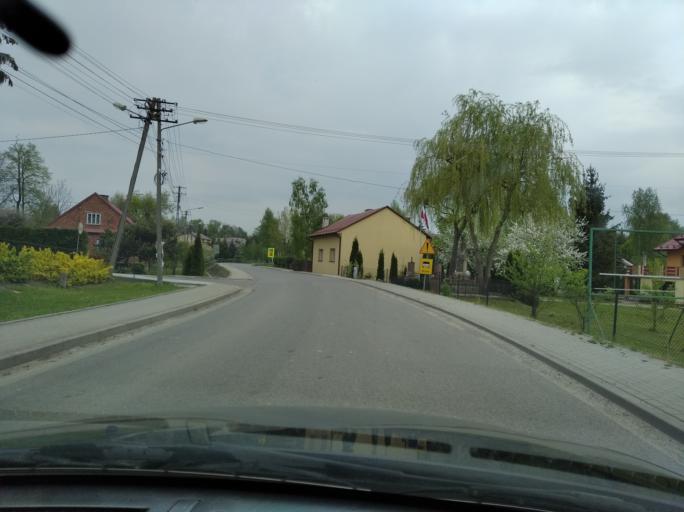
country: PL
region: Lesser Poland Voivodeship
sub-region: Powiat tarnowski
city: Skrzyszow
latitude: 49.9753
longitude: 21.0624
